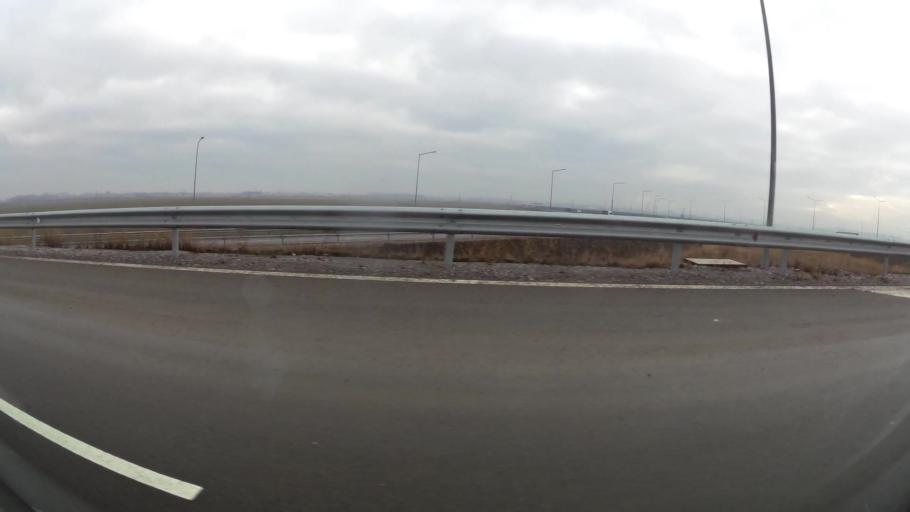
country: BG
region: Sofia-Capital
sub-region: Stolichna Obshtina
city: Sofia
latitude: 42.7689
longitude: 23.2904
